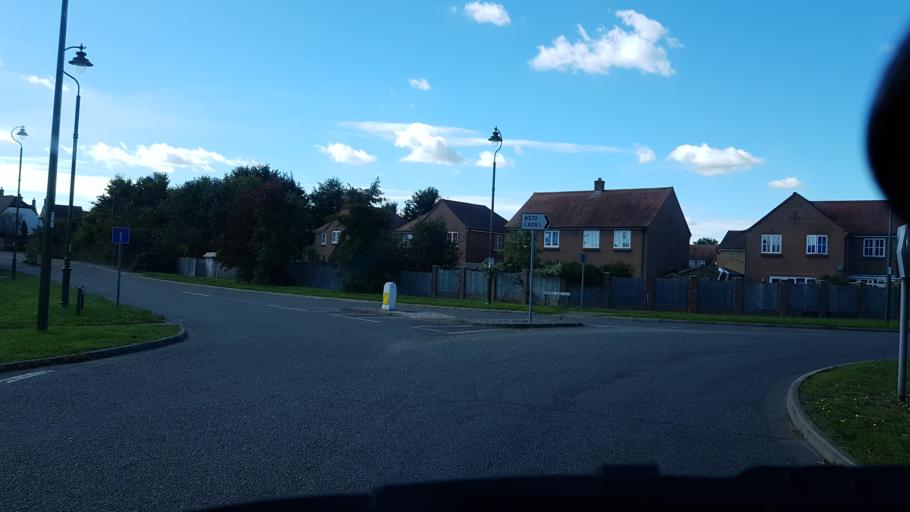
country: GB
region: England
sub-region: West Sussex
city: Billingshurst
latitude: 51.0222
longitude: -0.4582
